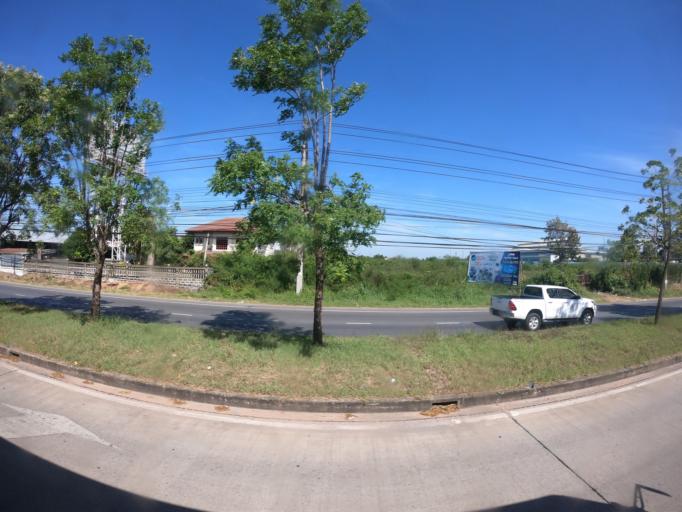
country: TH
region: Nakhon Ratchasima
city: Nakhon Ratchasima
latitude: 14.9976
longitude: 102.1126
